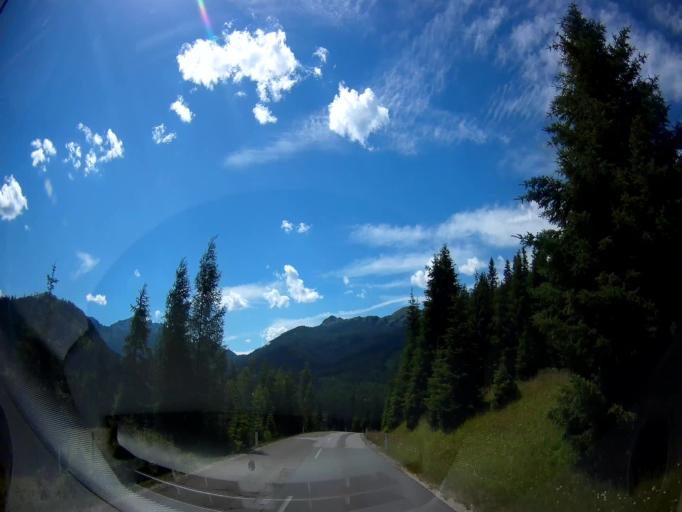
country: AT
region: Styria
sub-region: Politischer Bezirk Murau
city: Stadl an der Mur
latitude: 46.9717
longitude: 14.0147
